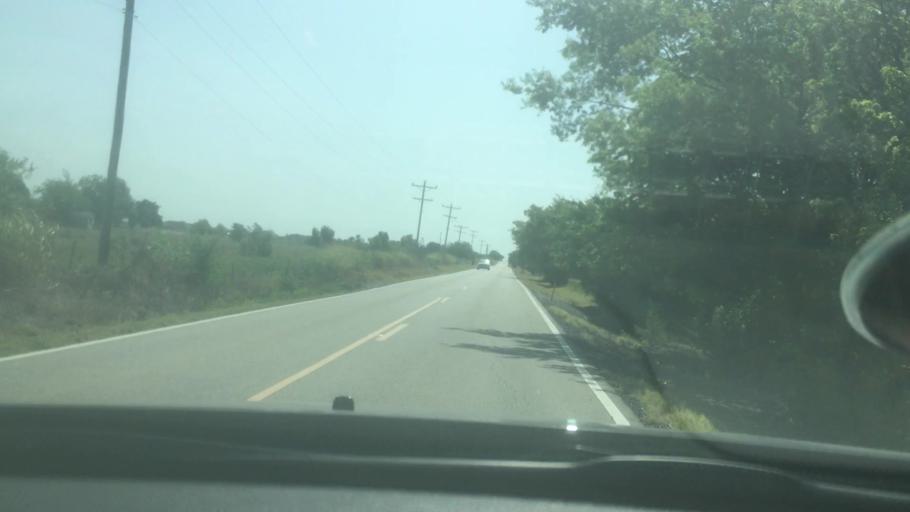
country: US
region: Oklahoma
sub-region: Bryan County
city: Durant
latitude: 34.0848
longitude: -96.4313
